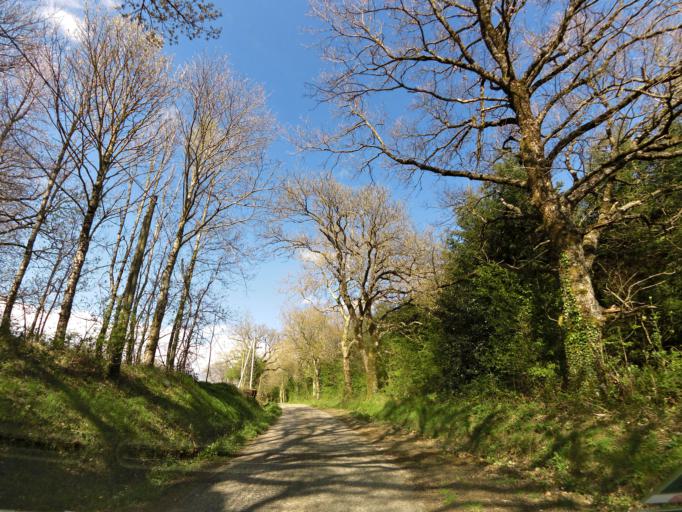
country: FR
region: Midi-Pyrenees
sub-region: Departement du Tarn
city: Soreze
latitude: 43.3866
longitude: 2.0729
